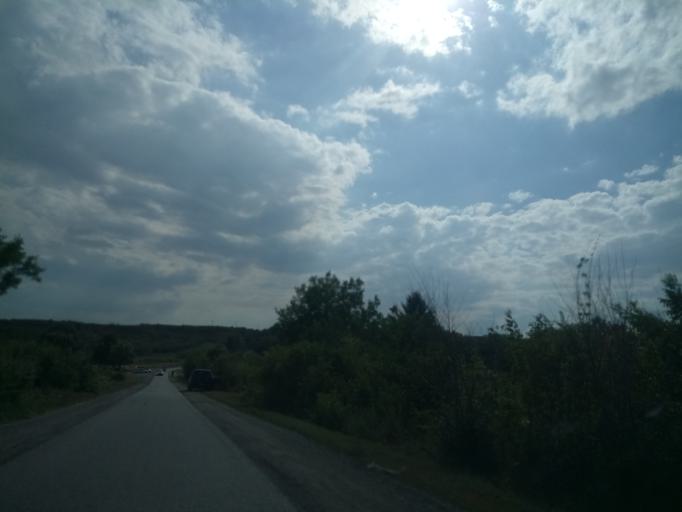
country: RS
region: Autonomna Pokrajina Vojvodina
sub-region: Sremski Okrug
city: Irig
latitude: 45.1050
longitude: 19.9133
